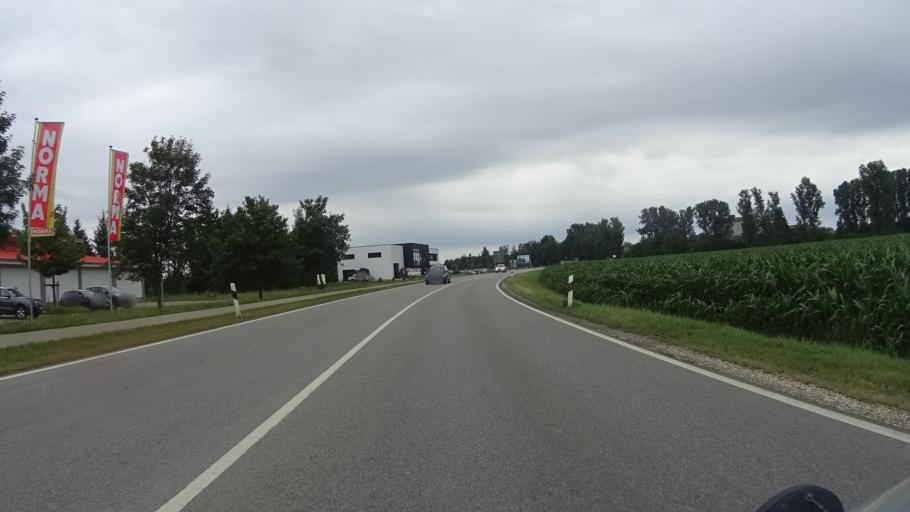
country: DE
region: Bavaria
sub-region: Swabia
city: Heimertingen
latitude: 48.0304
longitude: 10.1497
